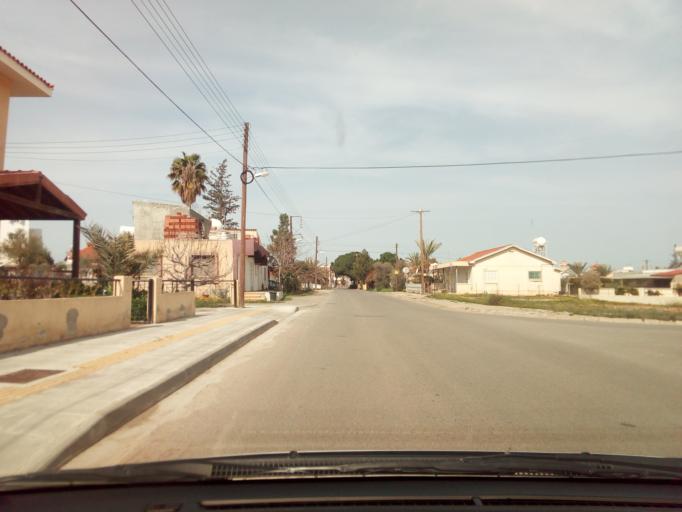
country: CY
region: Lefkosia
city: Tseri
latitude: 35.1024
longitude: 33.3055
